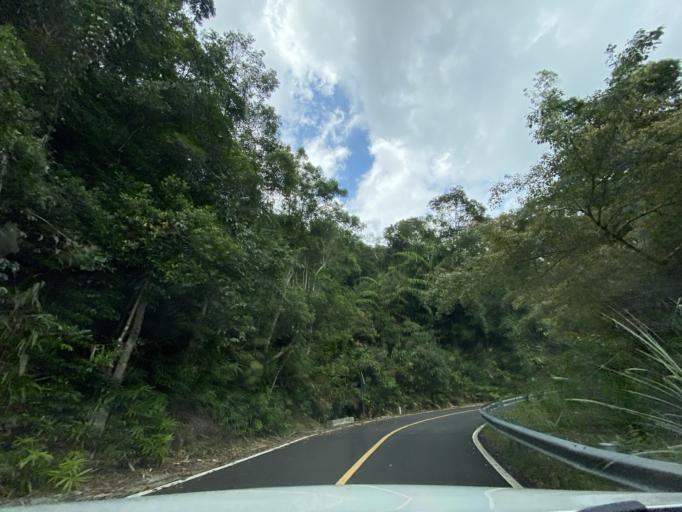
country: CN
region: Hainan
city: Benhao
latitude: 18.6819
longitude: 109.8785
